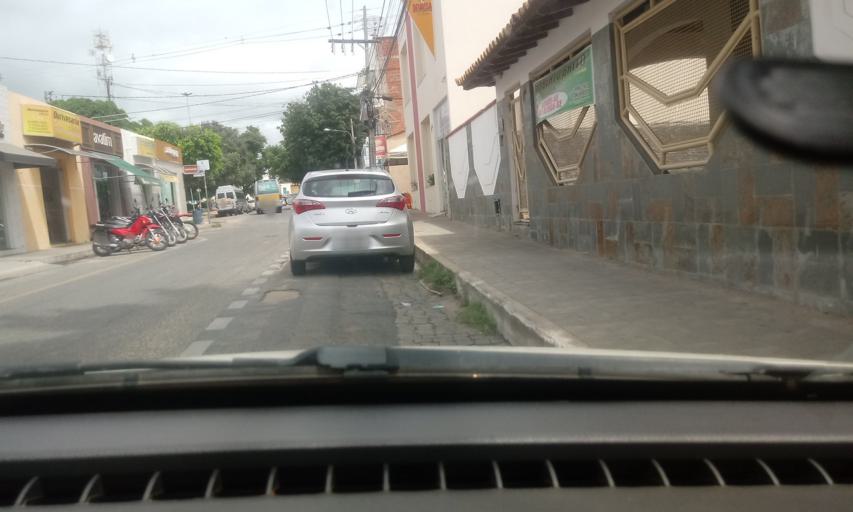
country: BR
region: Bahia
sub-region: Guanambi
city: Guanambi
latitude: -14.2255
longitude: -42.7804
